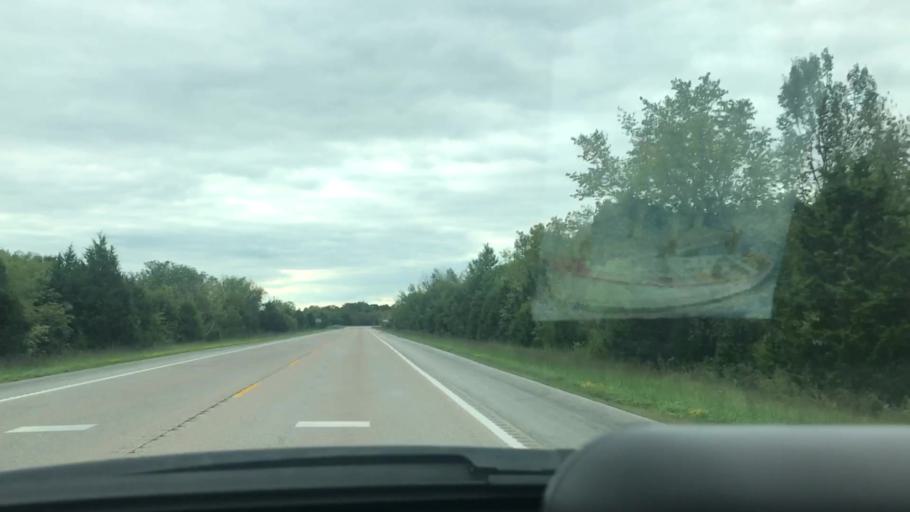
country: US
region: Missouri
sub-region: Benton County
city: Warsaw
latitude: 38.2105
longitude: -93.3376
